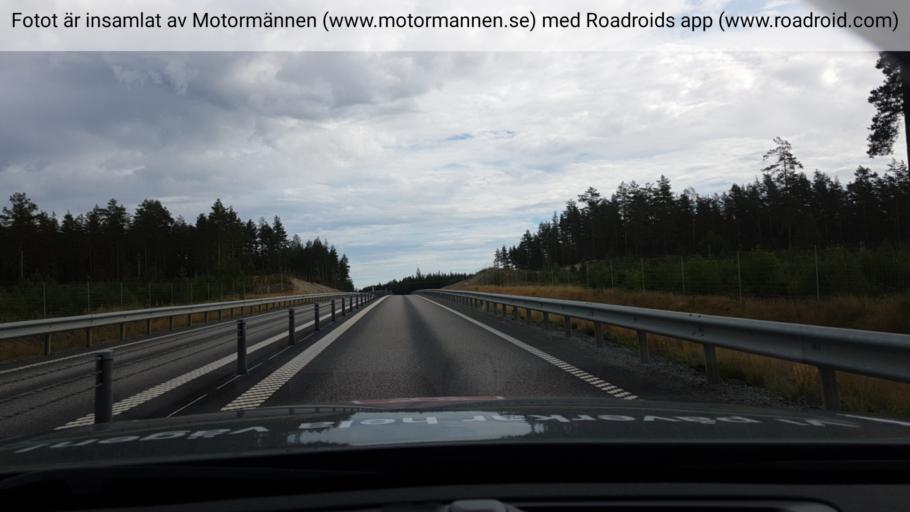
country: SE
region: Uppsala
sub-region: Heby Kommun
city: Heby
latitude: 59.9745
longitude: 16.8441
